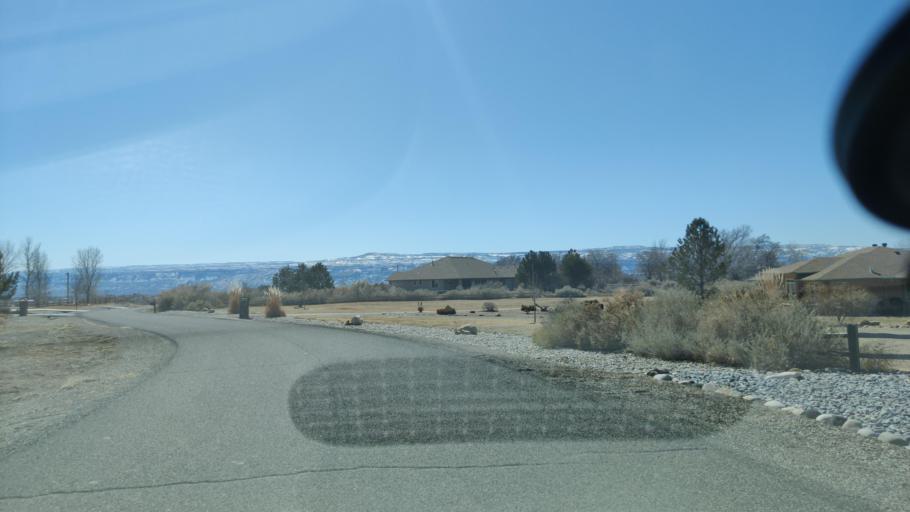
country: US
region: Colorado
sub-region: Mesa County
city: Fruita
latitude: 39.2058
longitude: -108.7137
